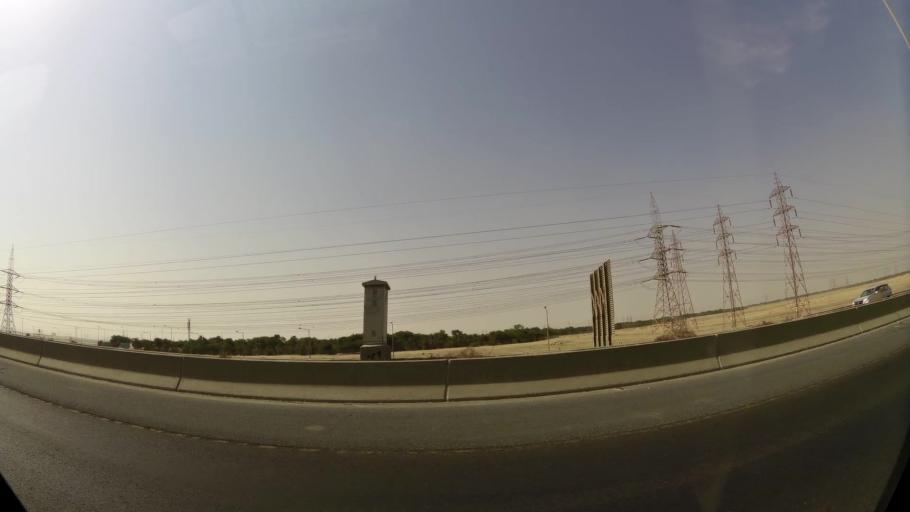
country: KW
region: Al Ahmadi
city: Al Fahahil
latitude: 29.0493
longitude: 48.1125
